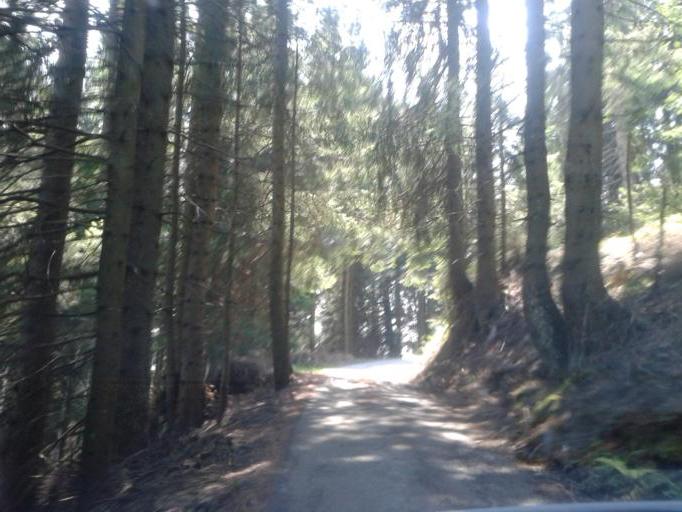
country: IT
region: Trentino-Alto Adige
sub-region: Provincia di Trento
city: Lodrone-Darzo
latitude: 45.8626
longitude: 10.5325
